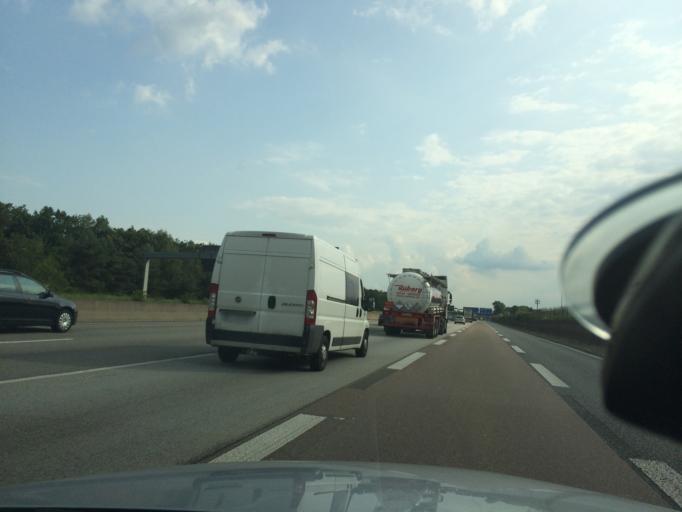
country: DE
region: Hesse
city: Niederrad
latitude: 50.0442
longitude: 8.5995
